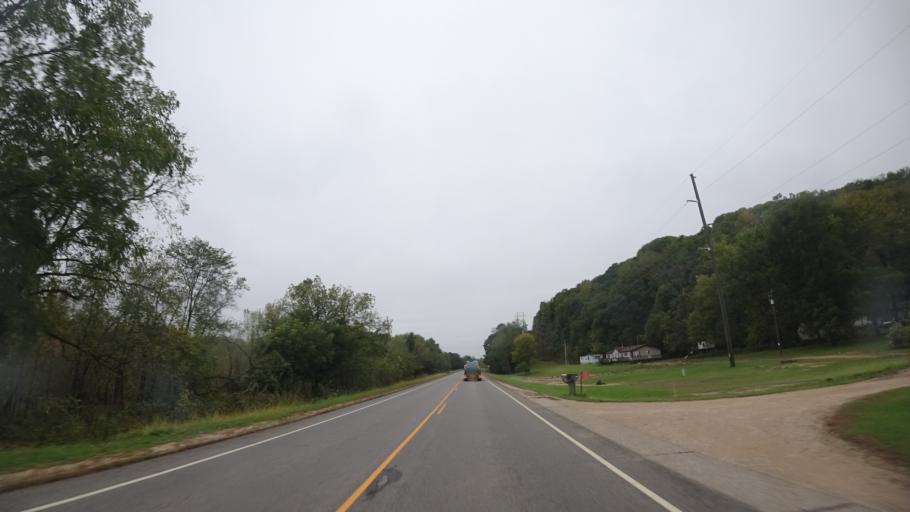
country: US
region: Wisconsin
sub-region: Crawford County
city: Prairie du Chien
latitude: 43.0668
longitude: -90.9486
